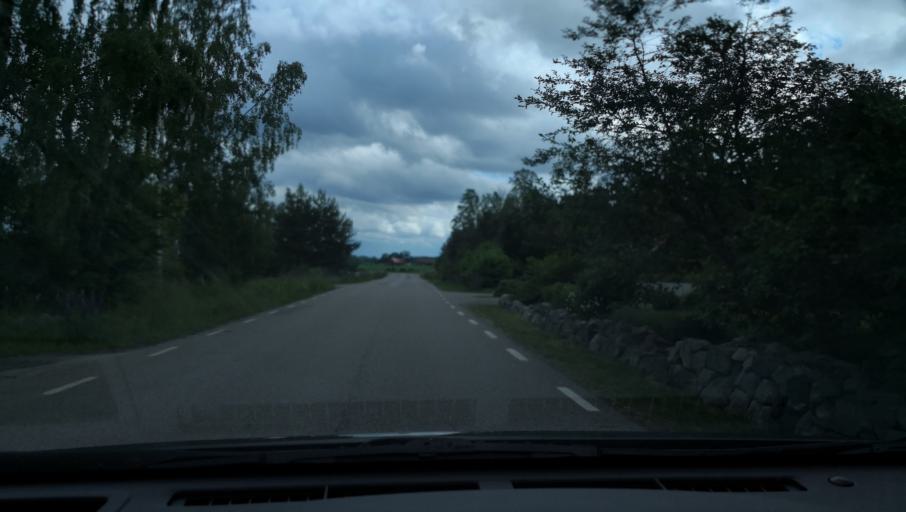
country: SE
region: OErebro
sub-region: Lindesbergs Kommun
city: Fellingsbro
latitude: 59.3263
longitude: 15.6771
